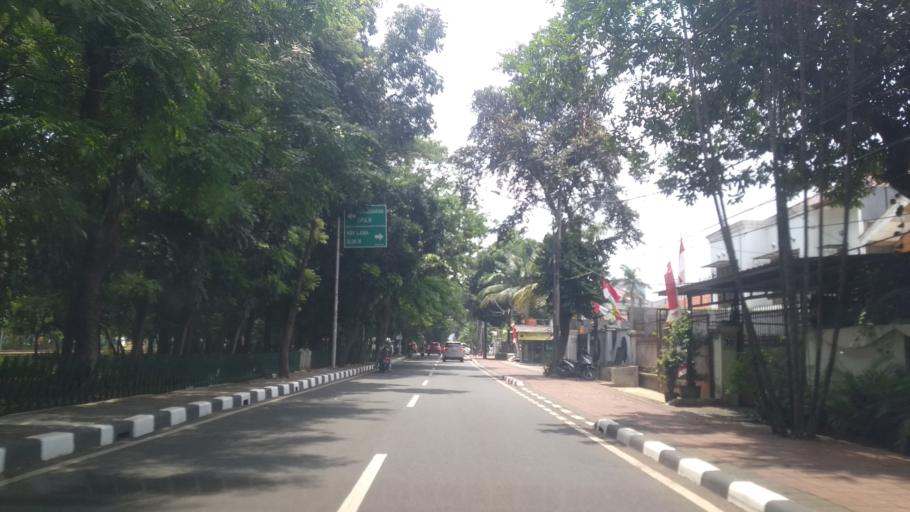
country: ID
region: Banten
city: South Tangerang
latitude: -6.2502
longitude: 106.7736
